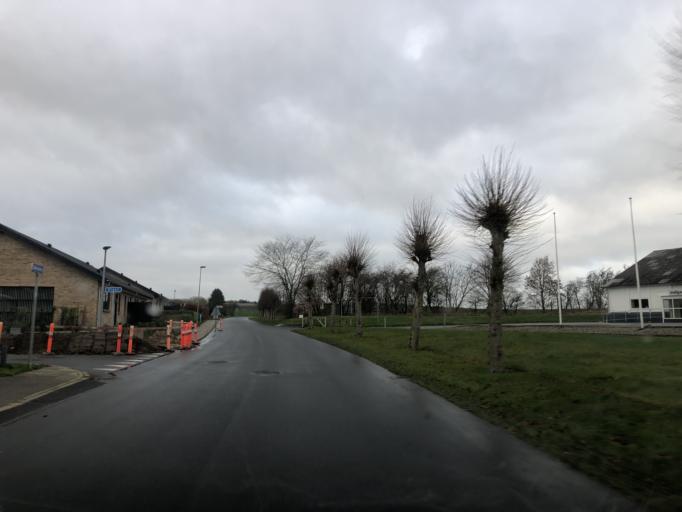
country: DK
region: North Denmark
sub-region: Vesthimmerland Kommune
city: Alestrup
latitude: 56.5922
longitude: 9.6226
